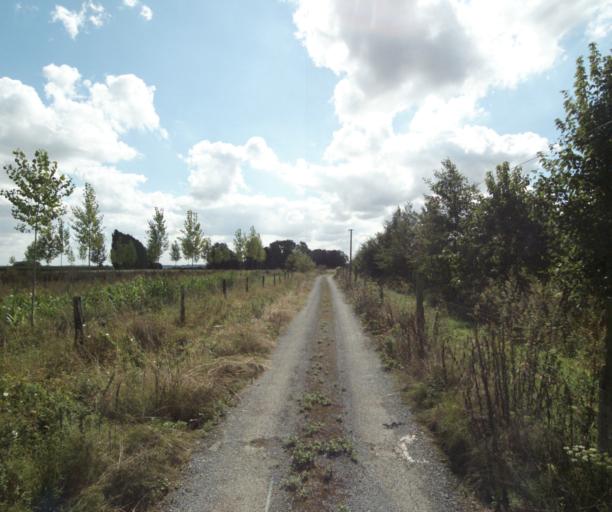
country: FR
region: Nord-Pas-de-Calais
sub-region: Departement du Nord
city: Willems
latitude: 50.6376
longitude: 3.2435
